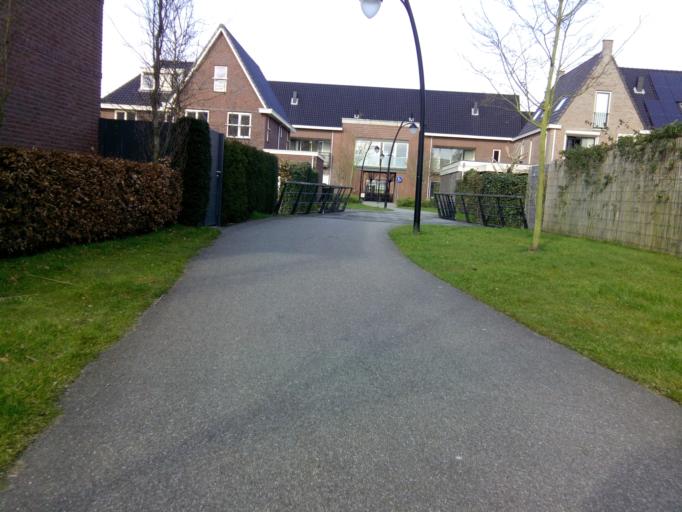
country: NL
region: Utrecht
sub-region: Gemeente Leusden
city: Leusden
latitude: 52.1197
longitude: 5.4110
